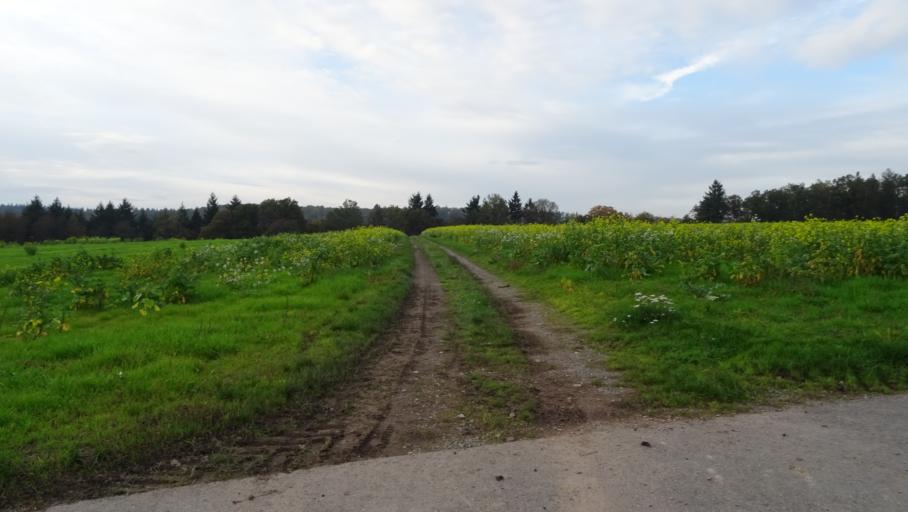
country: DE
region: Baden-Wuerttemberg
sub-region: Karlsruhe Region
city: Binau
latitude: 49.3737
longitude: 9.0713
